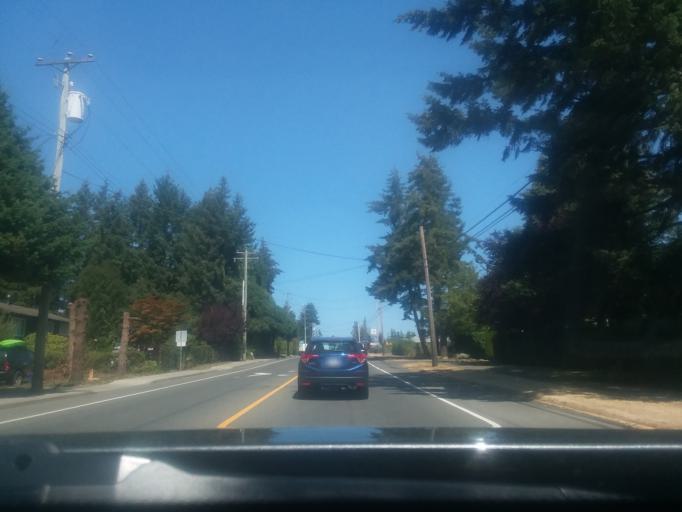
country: CA
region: British Columbia
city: Courtenay
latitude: 49.6848
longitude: -124.9351
